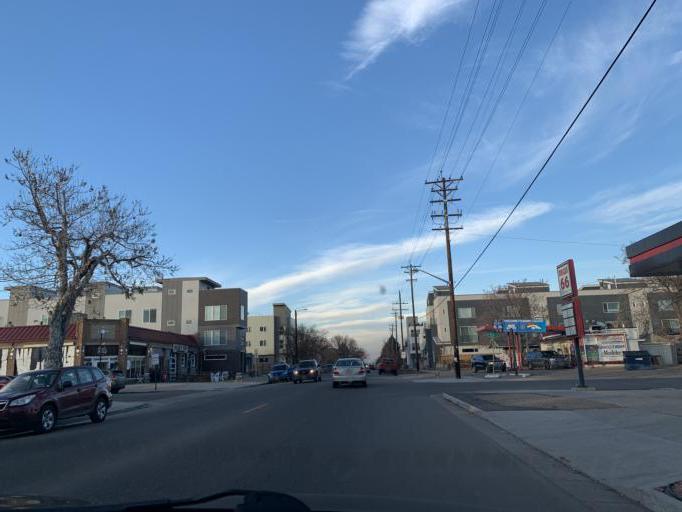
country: US
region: Colorado
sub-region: Adams County
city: Berkley
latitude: 39.7853
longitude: -105.0345
